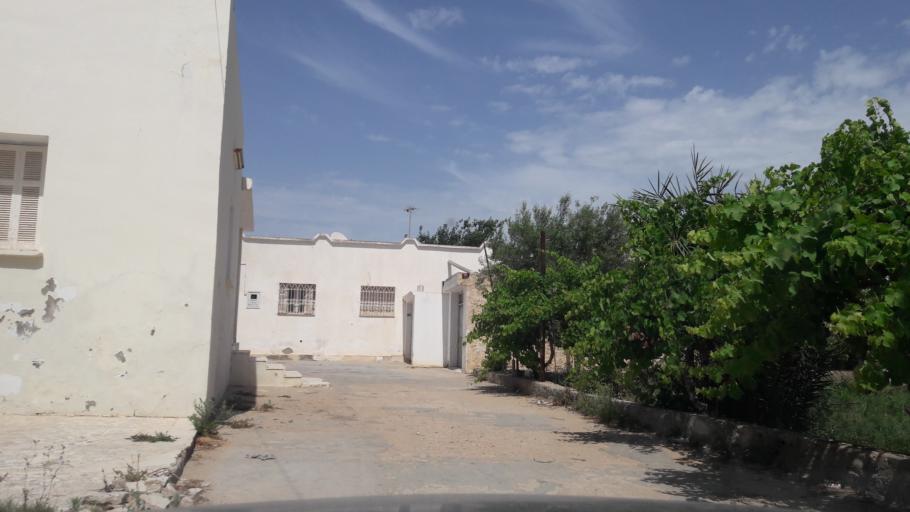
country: TN
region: Safaqis
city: Al Qarmadah
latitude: 34.7762
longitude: 10.7711
